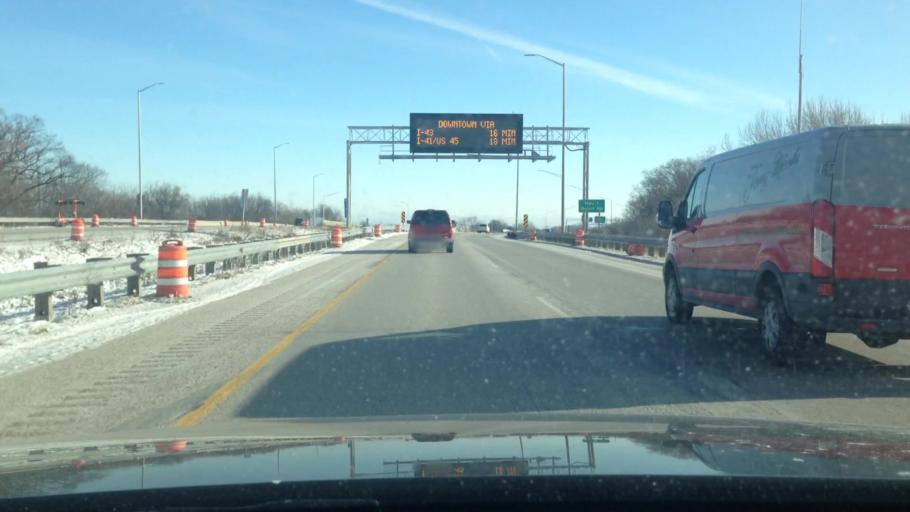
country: US
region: Wisconsin
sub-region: Waukesha County
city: New Berlin
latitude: 42.9586
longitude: -88.0811
